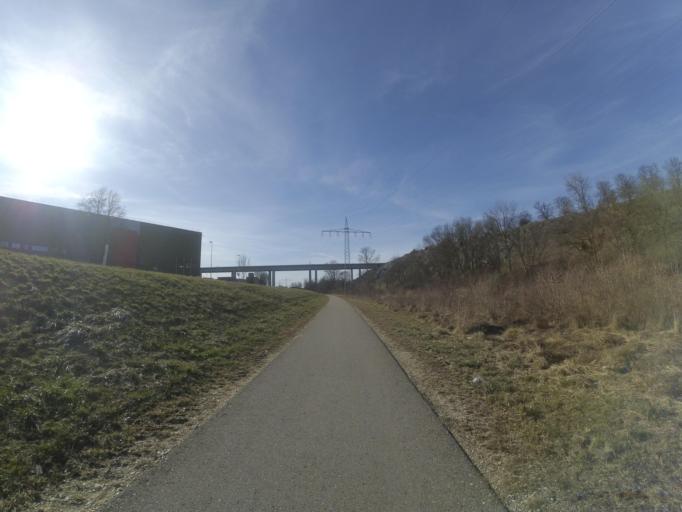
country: DE
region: Baden-Wuerttemberg
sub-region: Regierungsbezirk Stuttgart
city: Giengen an der Brenz
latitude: 48.6265
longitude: 10.2258
